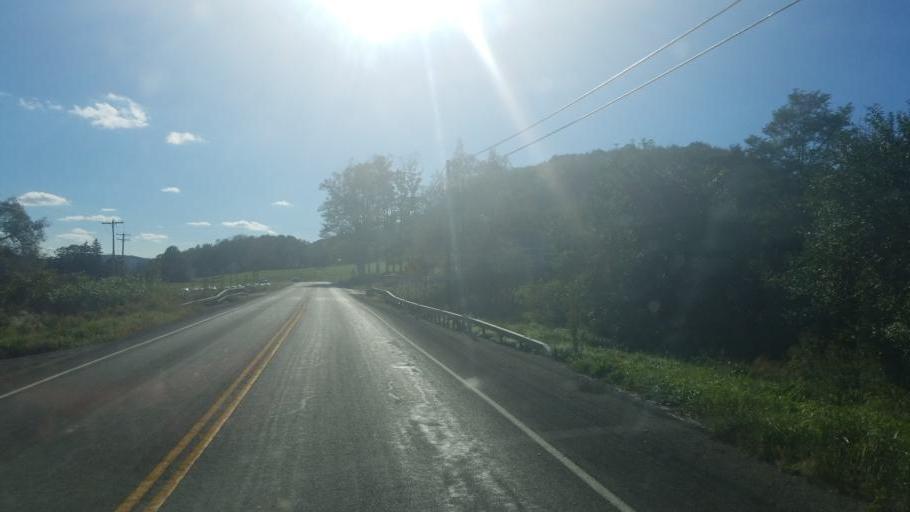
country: US
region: New York
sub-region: Allegany County
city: Cuba
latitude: 42.2678
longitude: -78.2526
